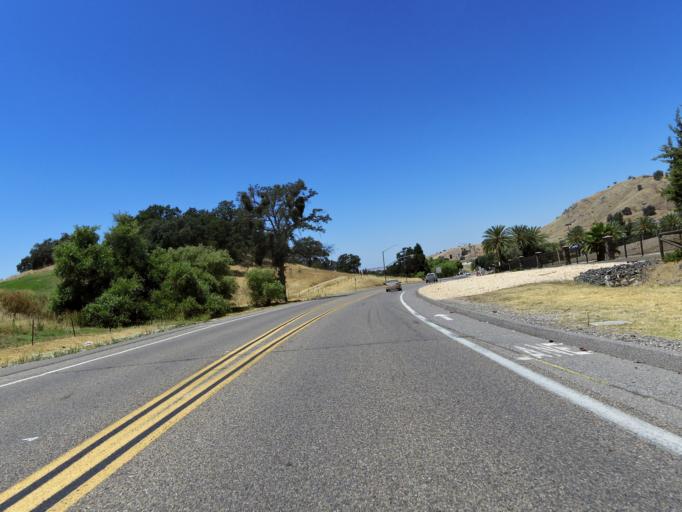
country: US
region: California
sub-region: Fresno County
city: Clovis
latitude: 36.9823
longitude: -119.6376
